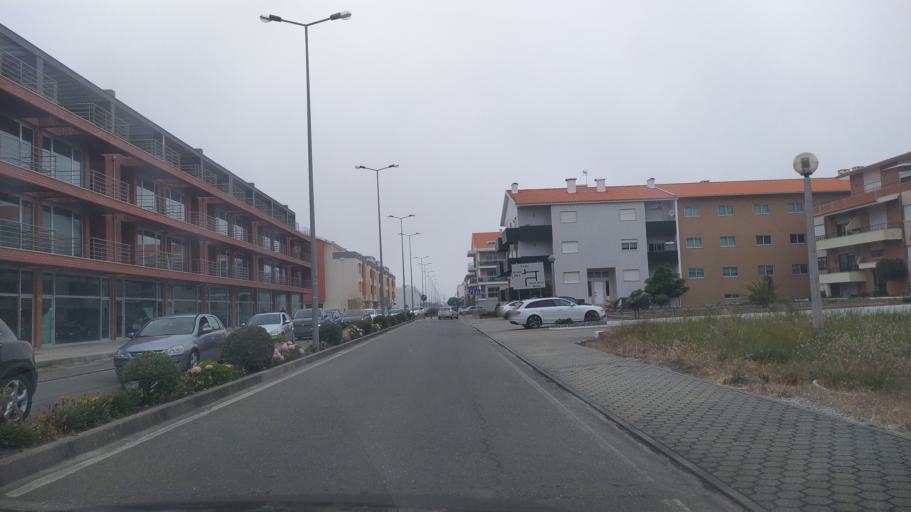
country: PT
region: Aveiro
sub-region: Ilhavo
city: Gafanha da Encarnacao
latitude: 40.5612
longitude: -8.7609
